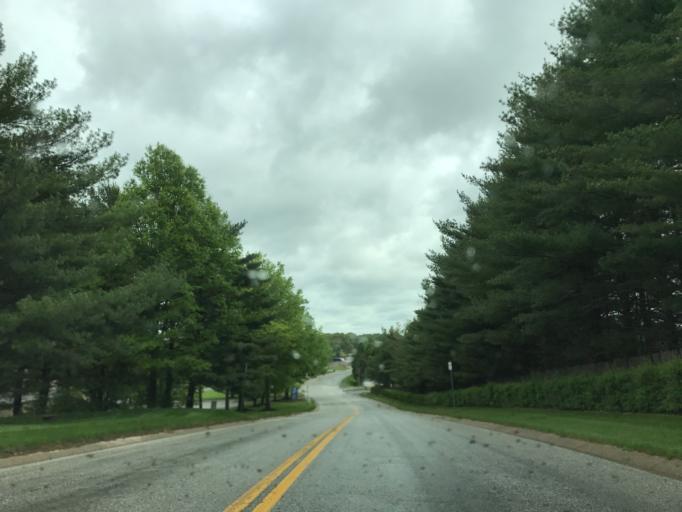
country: US
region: Maryland
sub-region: Baltimore County
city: Reisterstown
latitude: 39.4932
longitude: -76.8835
